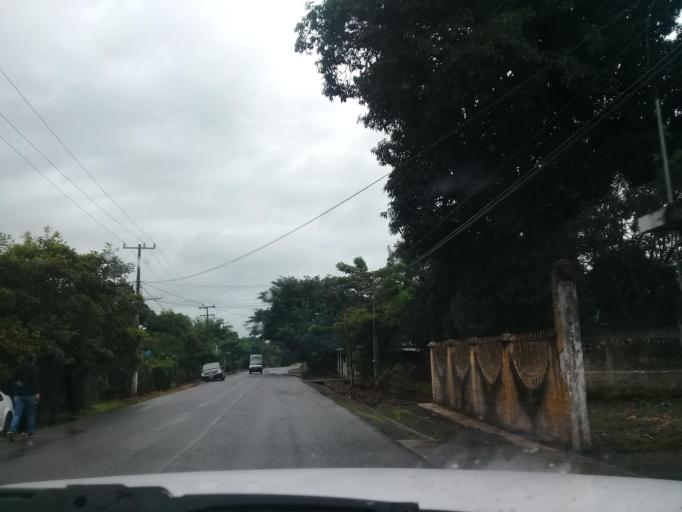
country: MX
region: Veracruz
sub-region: San Andres Tuxtla
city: Cerro las Iguanas
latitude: 18.4231
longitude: -95.2177
